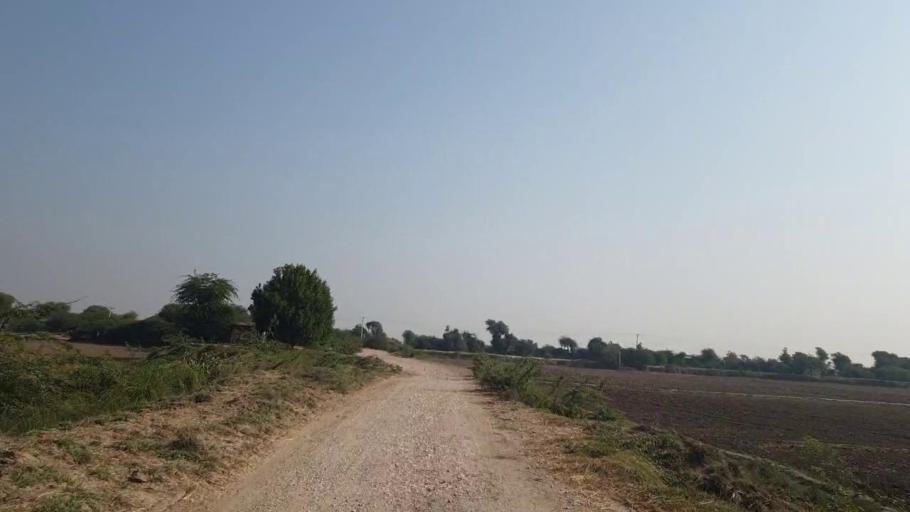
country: PK
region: Sindh
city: Matli
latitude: 25.0067
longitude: 68.6301
